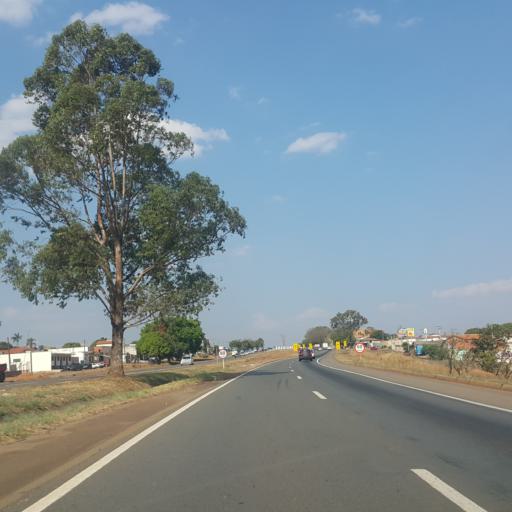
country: BR
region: Goias
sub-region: Abadiania
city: Abadiania
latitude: -16.1881
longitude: -48.7171
